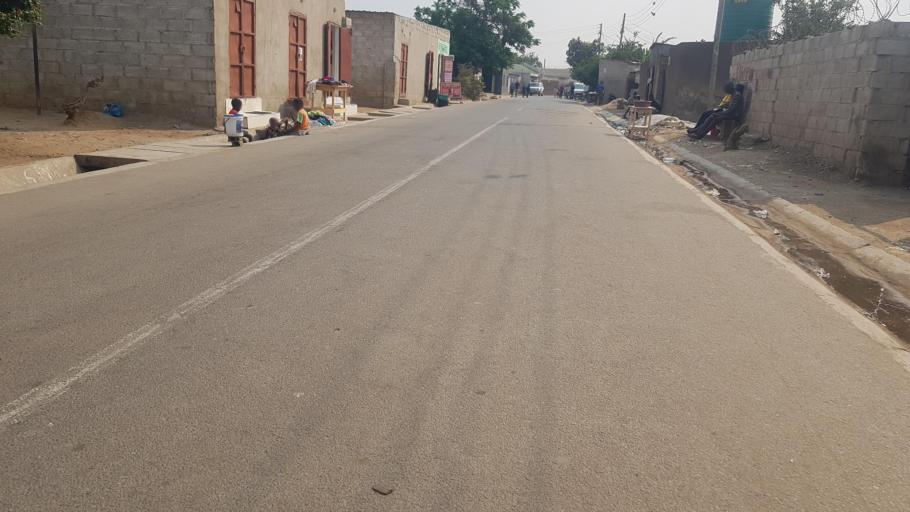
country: ZM
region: Lusaka
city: Lusaka
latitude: -15.4455
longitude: 28.3749
